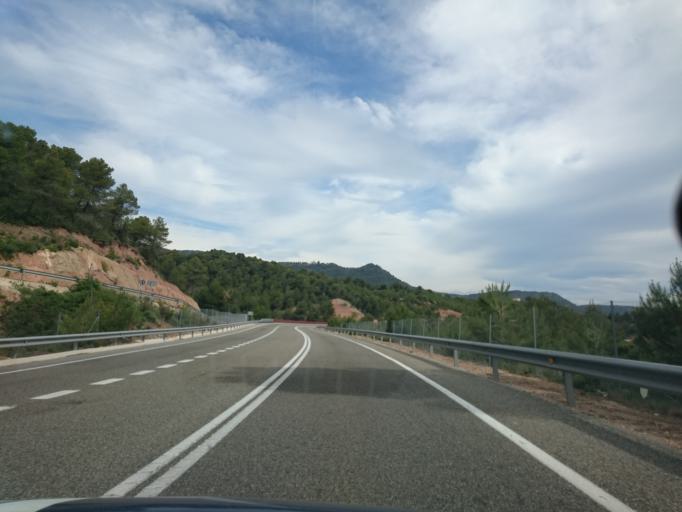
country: ES
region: Catalonia
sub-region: Provincia de Barcelona
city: Castellfollit del Boix
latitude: 41.6496
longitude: 1.7077
